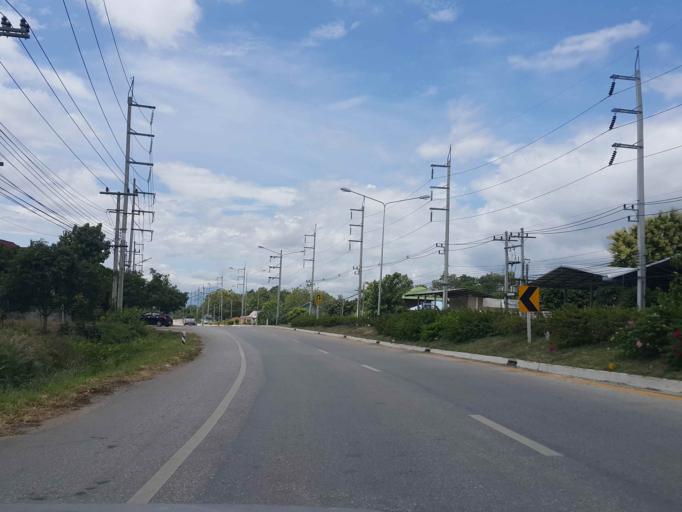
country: TH
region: Lamphun
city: Ban Hong
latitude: 18.3422
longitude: 98.8143
